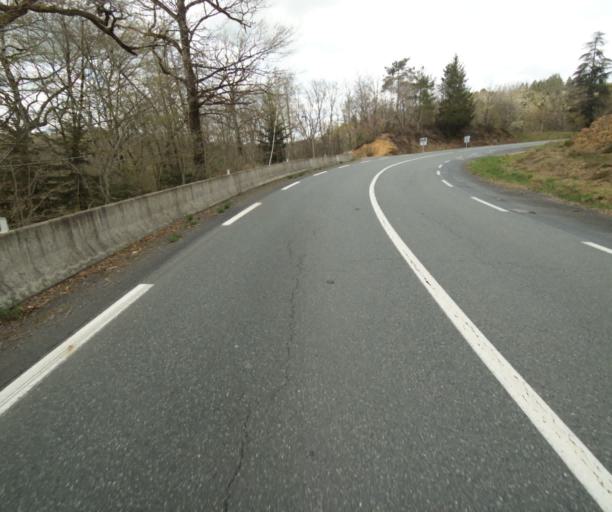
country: FR
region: Limousin
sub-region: Departement de la Correze
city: Sainte-Fortunade
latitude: 45.1890
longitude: 1.8429
